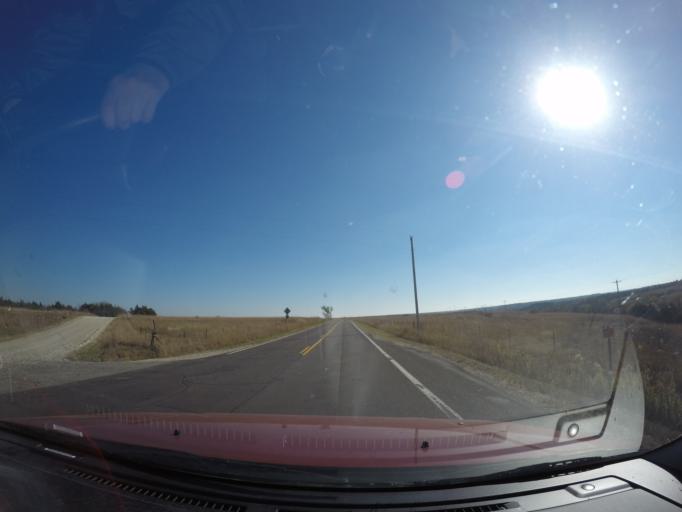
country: US
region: Kansas
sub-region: Geary County
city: Grandview Plaza
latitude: 39.0151
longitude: -96.7567
